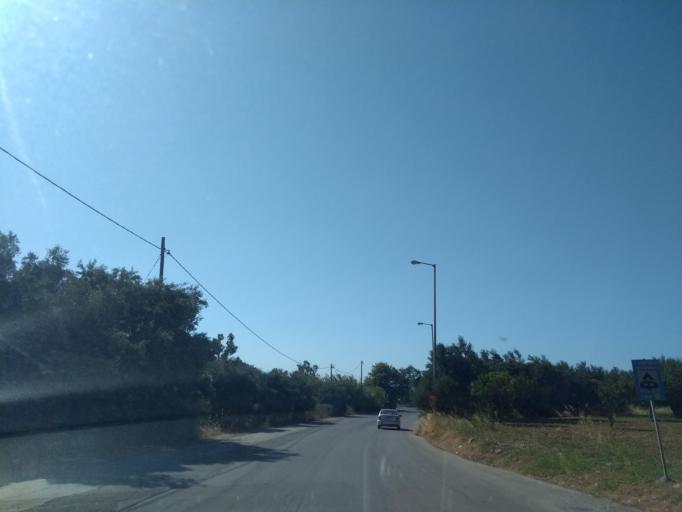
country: GR
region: Crete
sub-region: Nomos Chanias
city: Kissamos
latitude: 35.5009
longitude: 23.7152
